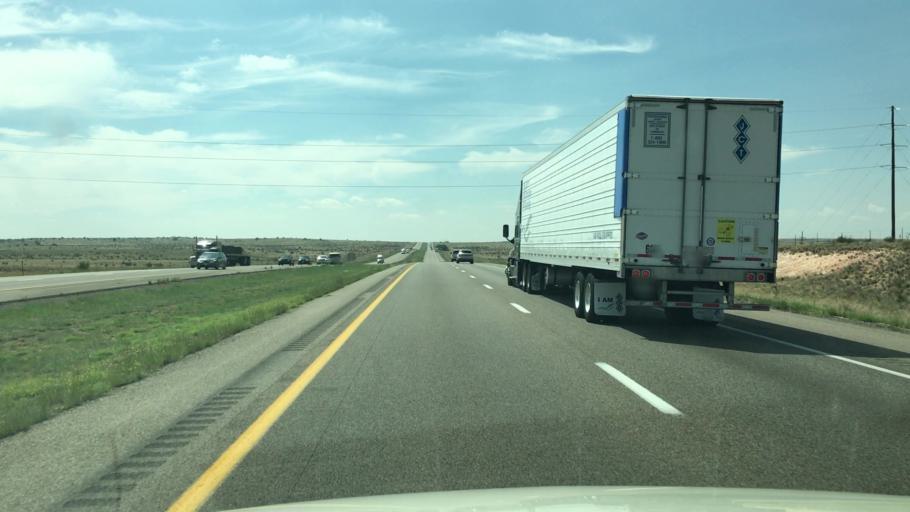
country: US
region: New Mexico
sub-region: Guadalupe County
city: Santa Rosa
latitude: 34.9783
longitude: -105.0243
